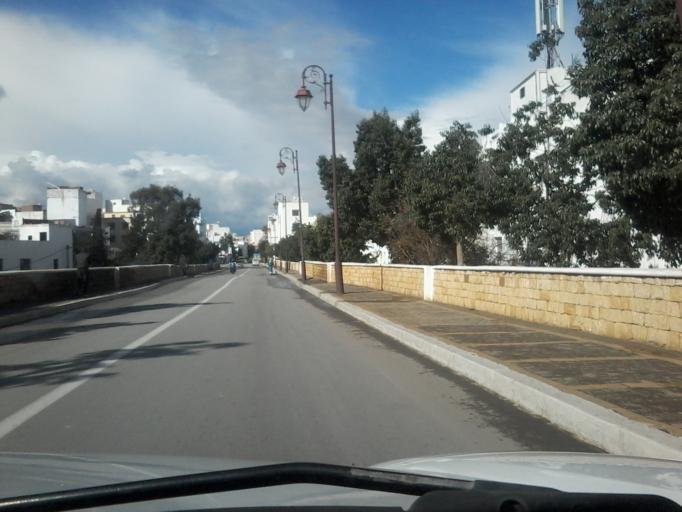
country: MA
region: Tanger-Tetouan
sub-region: Tetouan
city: Martil
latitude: 35.6831
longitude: -5.3281
